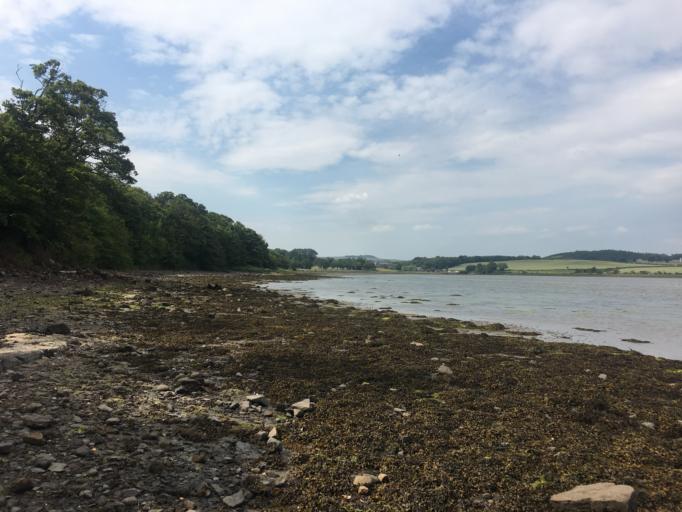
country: GB
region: England
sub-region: Northumberland
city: Bamburgh
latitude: 55.6087
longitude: -1.7586
